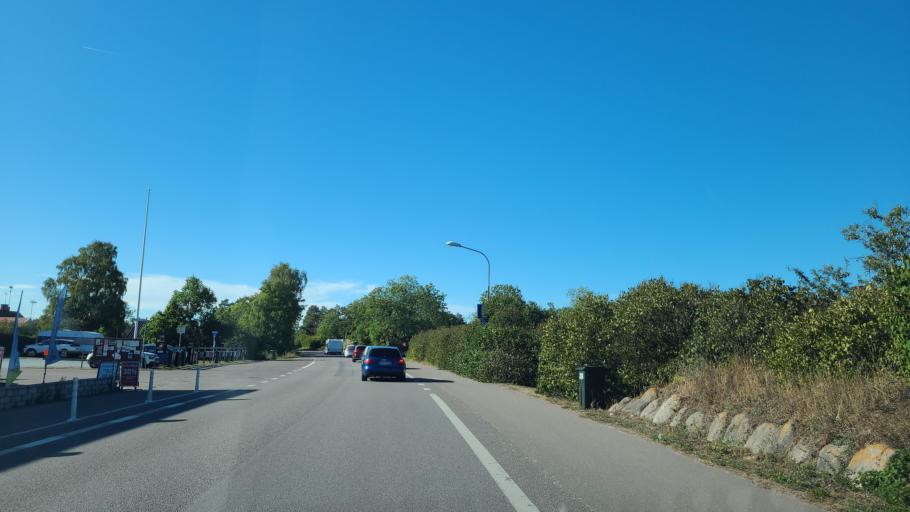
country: SE
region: Kalmar
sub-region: Borgholms Kommun
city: Borgholm
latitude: 57.2497
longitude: 17.0573
